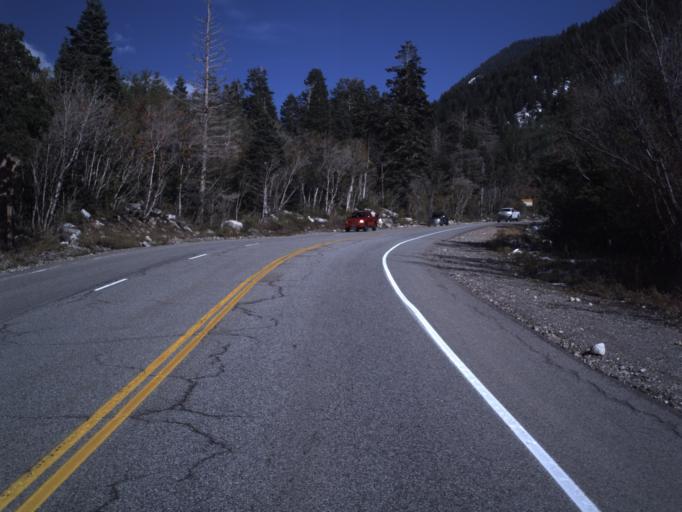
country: US
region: Utah
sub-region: Salt Lake County
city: Granite
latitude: 40.5711
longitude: -111.7054
